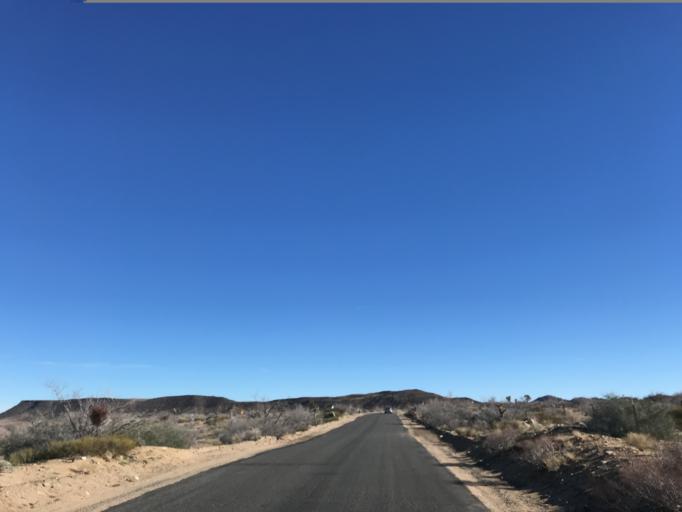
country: US
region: California
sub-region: San Bernardino County
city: Yucca Valley
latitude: 34.1828
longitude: -116.5379
